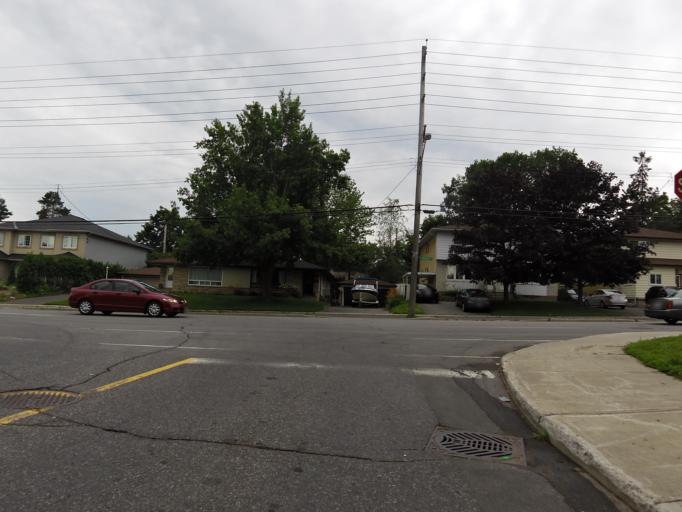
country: CA
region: Ontario
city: Bells Corners
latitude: 45.3534
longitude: -75.7917
